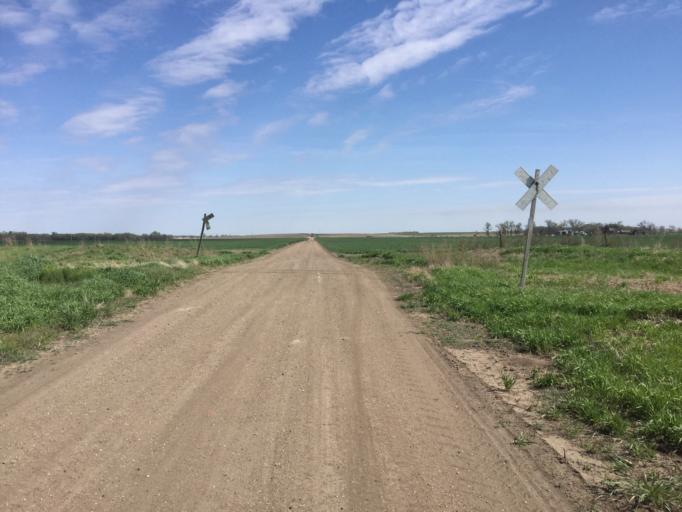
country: US
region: Kansas
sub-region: Osborne County
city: Osborne
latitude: 39.5174
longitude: -98.5908
